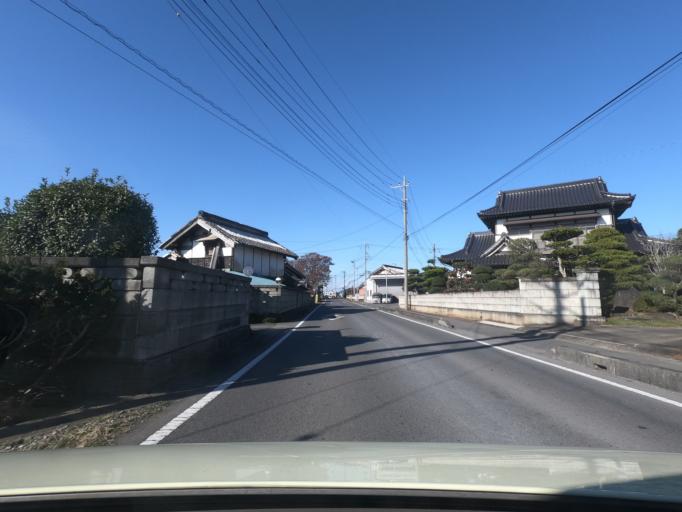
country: JP
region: Ibaraki
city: Ishige
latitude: 36.1603
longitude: 139.9944
